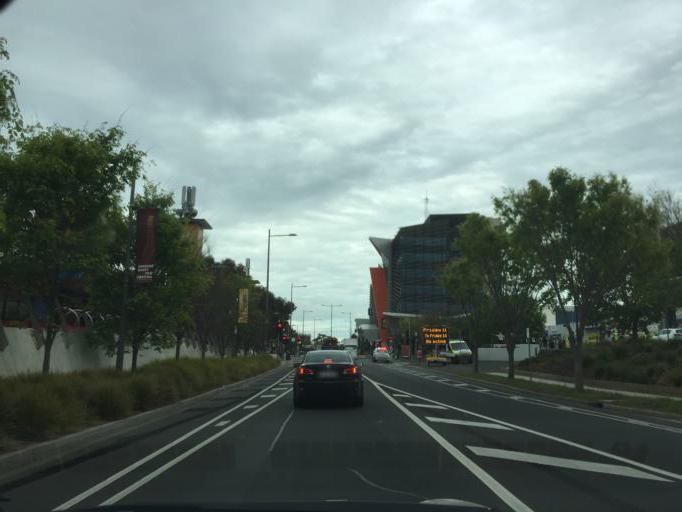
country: AU
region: Victoria
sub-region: Brimbank
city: Sunshine North
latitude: -37.7816
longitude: 144.8327
